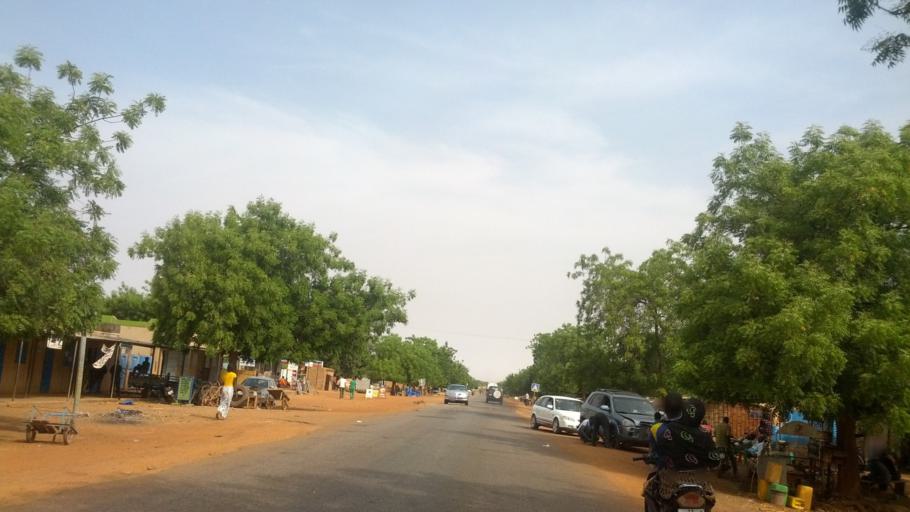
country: BF
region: Centre-Nord
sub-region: Province du Sanmatenga
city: Kaya
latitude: 12.9108
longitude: -1.0781
